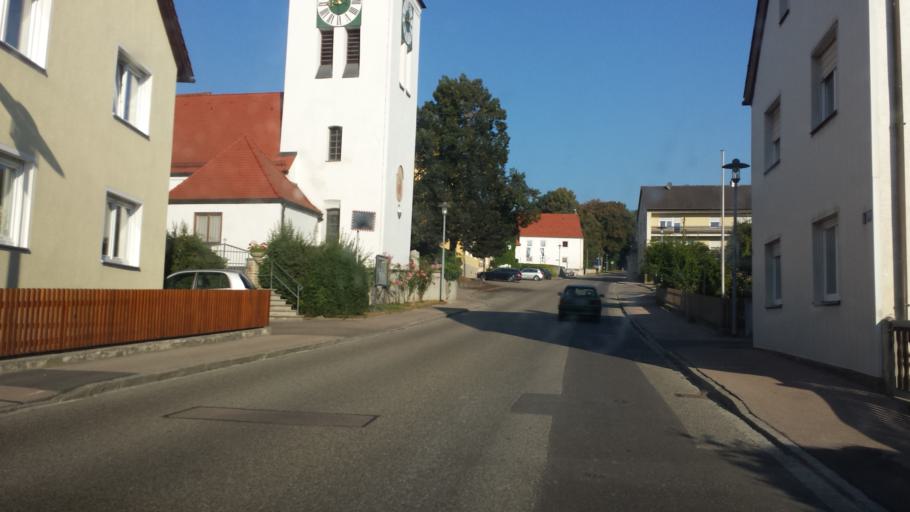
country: DE
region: Bavaria
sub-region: Upper Bavaria
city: Neuburg an der Donau
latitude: 48.7424
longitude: 11.1584
